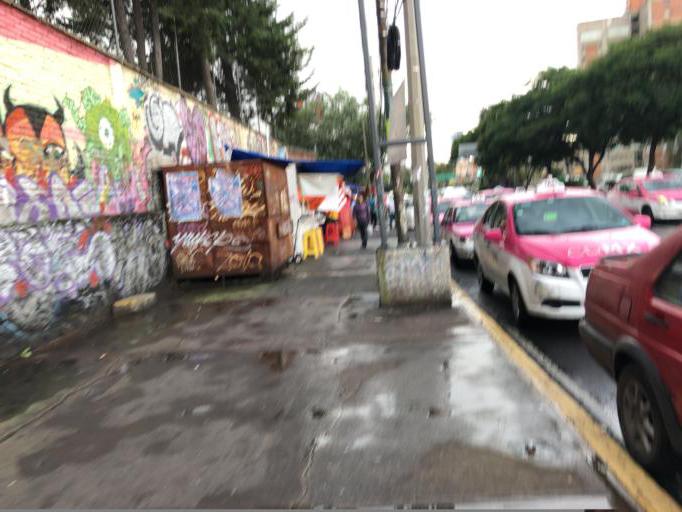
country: MX
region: Mexico City
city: Coyoacan
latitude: 19.3359
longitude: -99.1751
